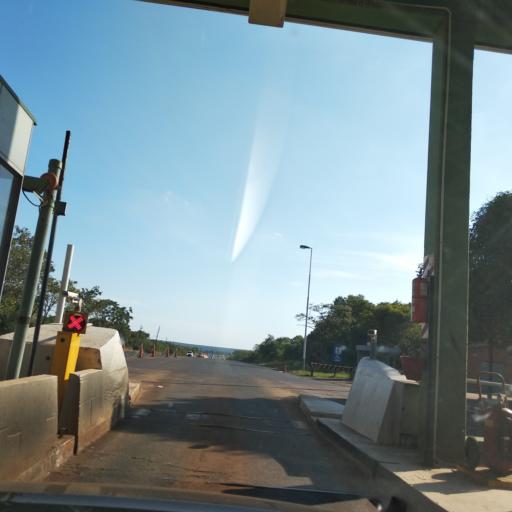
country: AR
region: Misiones
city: Santa Ana
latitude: -27.4284
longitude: -55.6297
